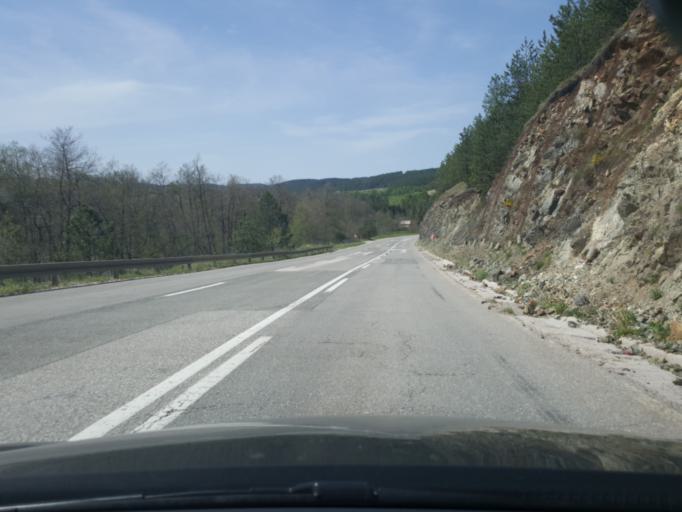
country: RS
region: Central Serbia
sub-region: Zlatiborski Okrug
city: Cajetina
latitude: 43.8366
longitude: 19.6061
